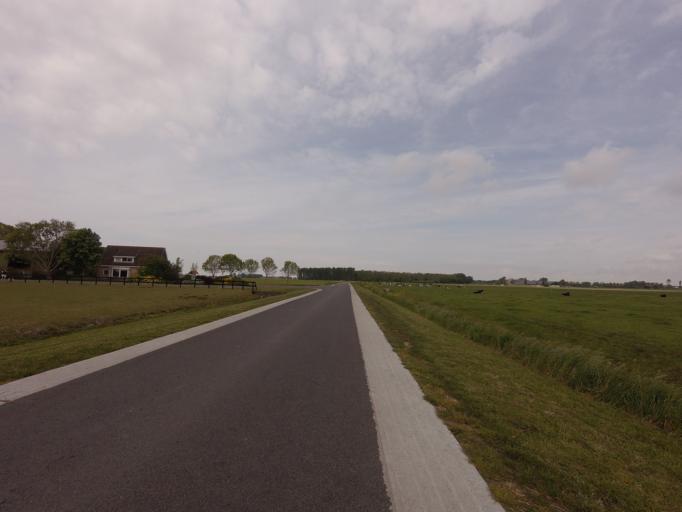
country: NL
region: Friesland
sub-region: Sudwest Fryslan
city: Bolsward
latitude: 53.0899
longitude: 5.4808
